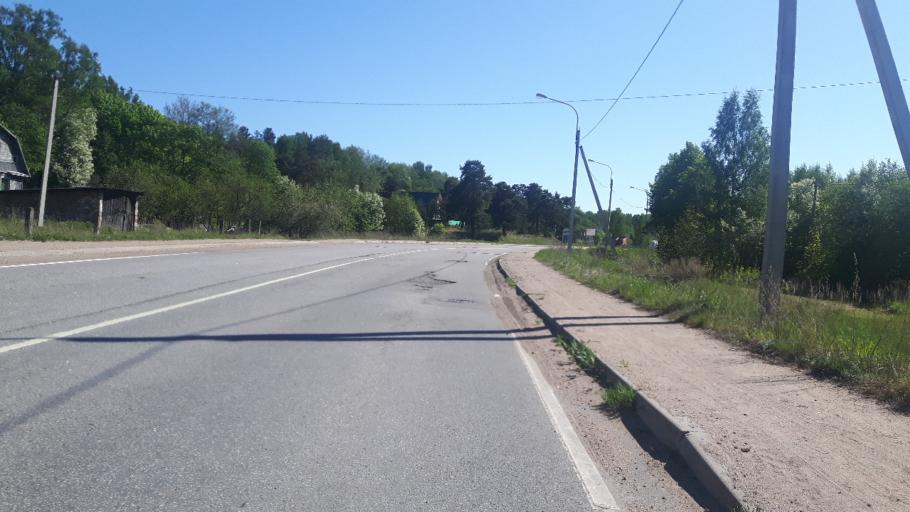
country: RU
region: Leningrad
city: Sosnovyy Bor
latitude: 60.2193
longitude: 29.0103
